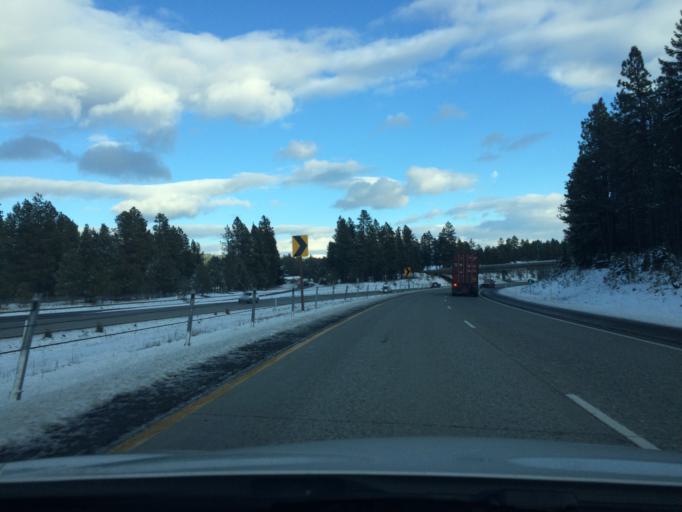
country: US
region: Washington
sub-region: Kittitas County
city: Cle Elum
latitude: 47.1947
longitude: -120.9620
